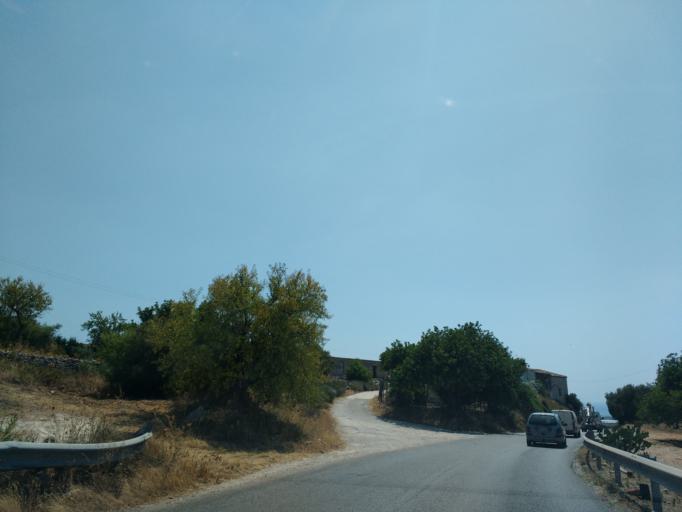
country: IT
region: Sicily
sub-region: Ragusa
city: Cava d'Aliga
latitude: 36.7596
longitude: 14.6896
